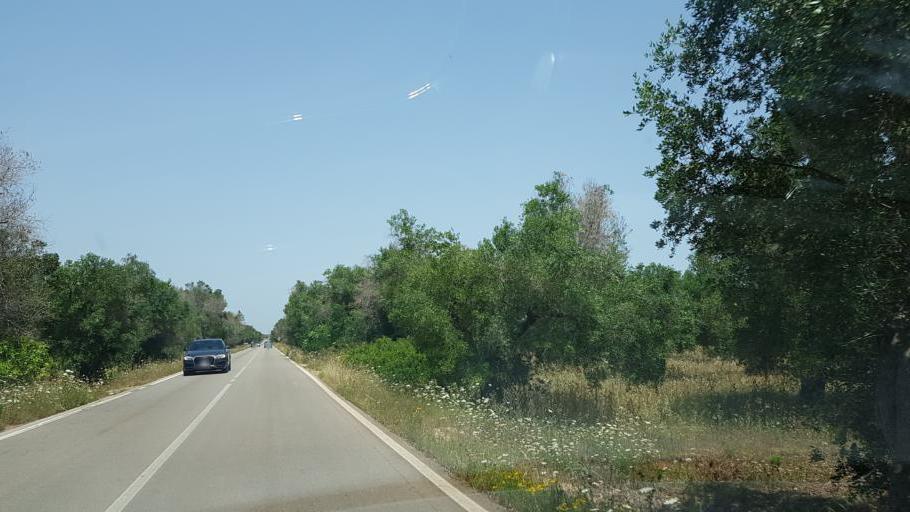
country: IT
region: Apulia
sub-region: Provincia di Lecce
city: Veglie
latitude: 40.3170
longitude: 17.9225
